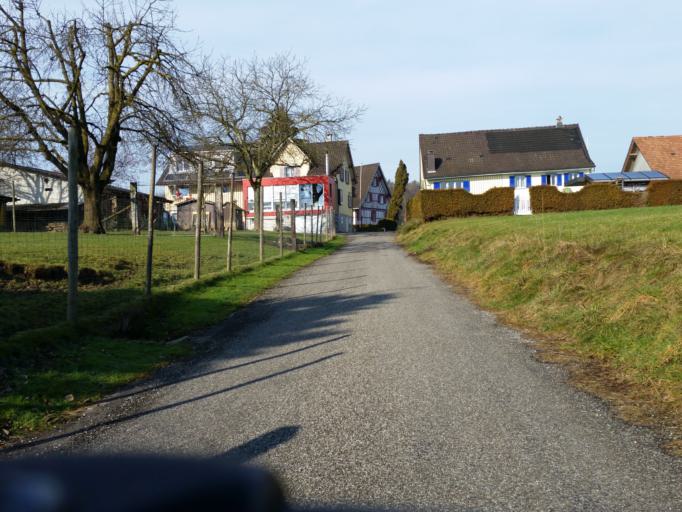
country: CH
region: Thurgau
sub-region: Arbon District
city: Salmsach
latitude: 47.5605
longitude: 9.3523
